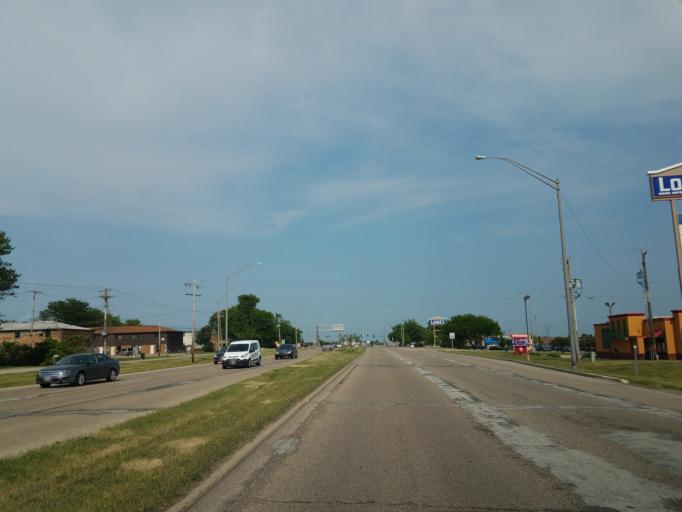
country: US
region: Illinois
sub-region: McLean County
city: Bloomington
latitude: 40.4881
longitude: -88.9489
